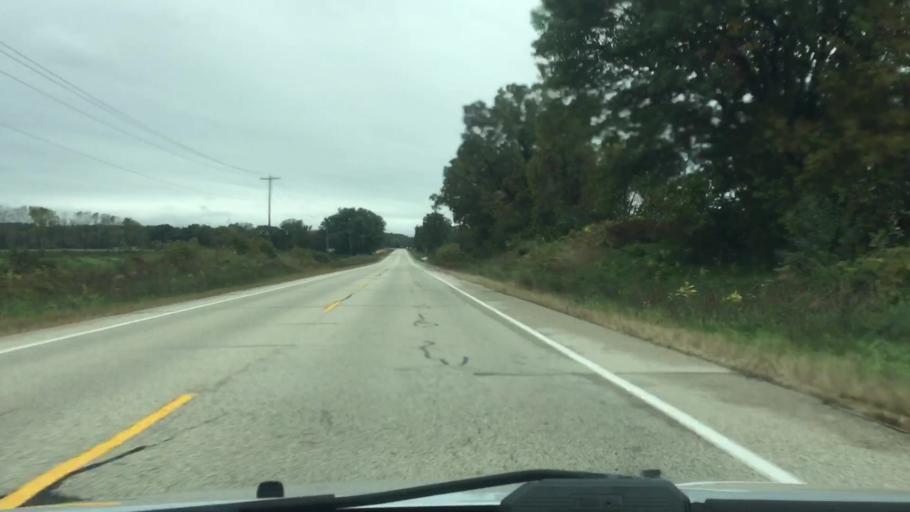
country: US
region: Wisconsin
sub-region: Jefferson County
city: Palmyra
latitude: 42.8252
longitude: -88.5539
